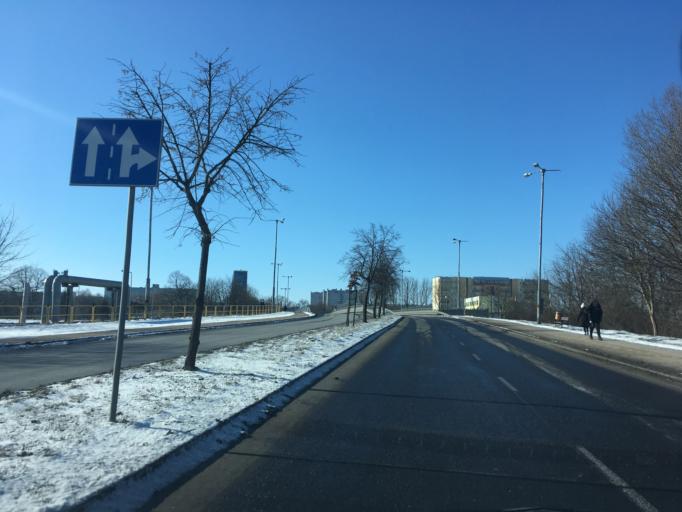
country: PL
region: Pomeranian Voivodeship
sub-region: Slupsk
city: Slupsk
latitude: 54.4723
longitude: 17.0190
